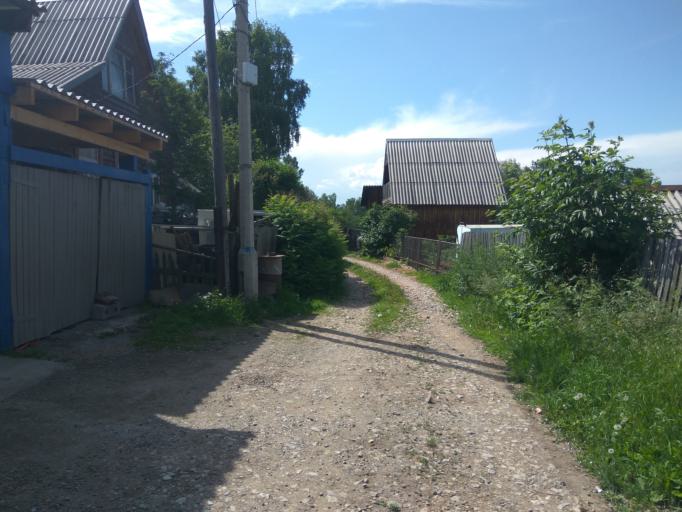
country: RU
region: Krasnoyarskiy
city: Krasnoyarsk
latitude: 55.9649
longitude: 92.8643
